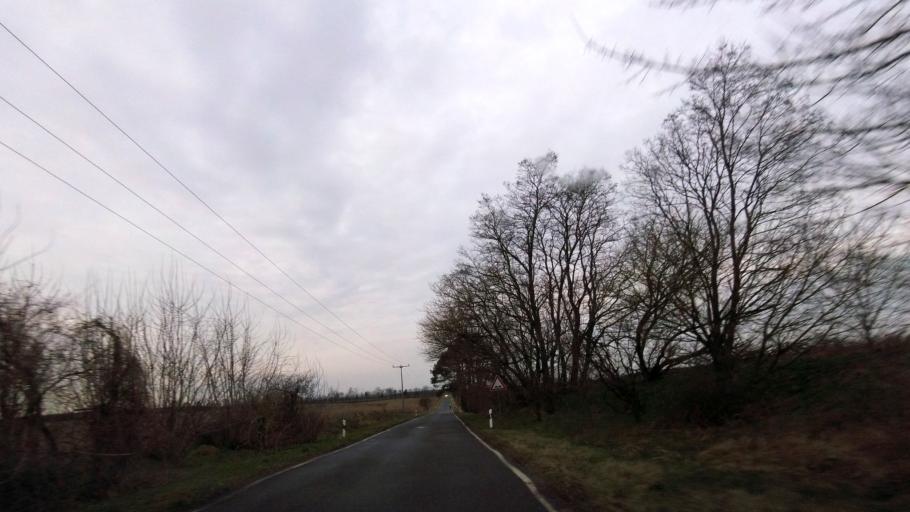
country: DE
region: Saxony-Anhalt
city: Seyda
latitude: 51.9167
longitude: 12.9557
